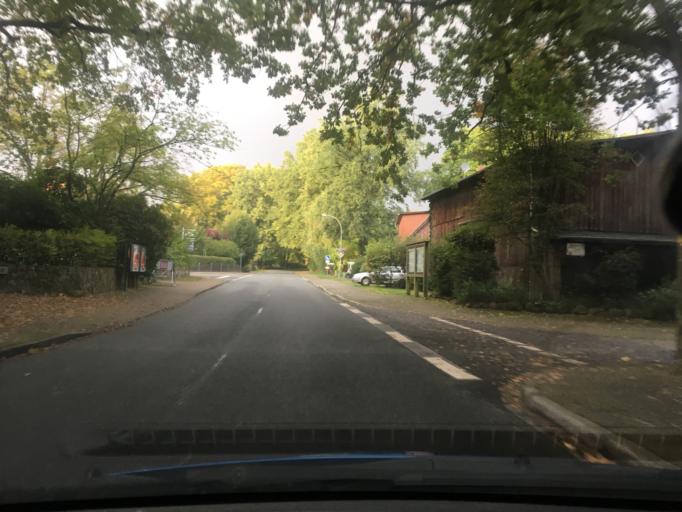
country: DE
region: Lower Saxony
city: Soderstorf
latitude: 53.1421
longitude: 10.1480
